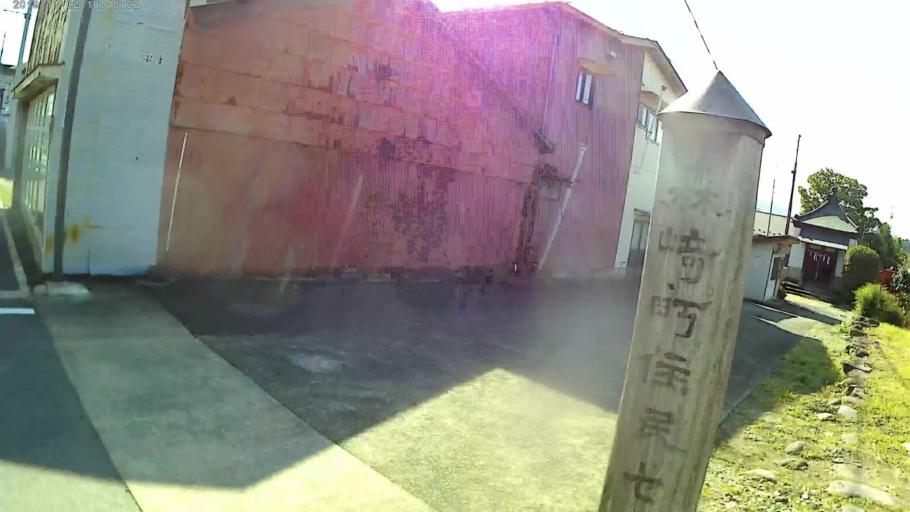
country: JP
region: Gunma
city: Annaka
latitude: 36.3149
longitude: 138.7971
